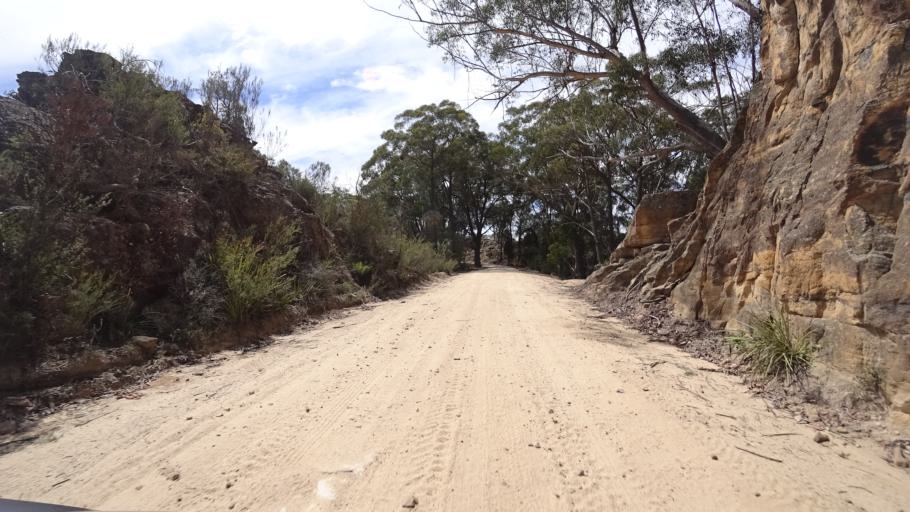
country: AU
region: New South Wales
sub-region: Lithgow
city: Lithgow
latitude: -33.2513
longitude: 150.2206
